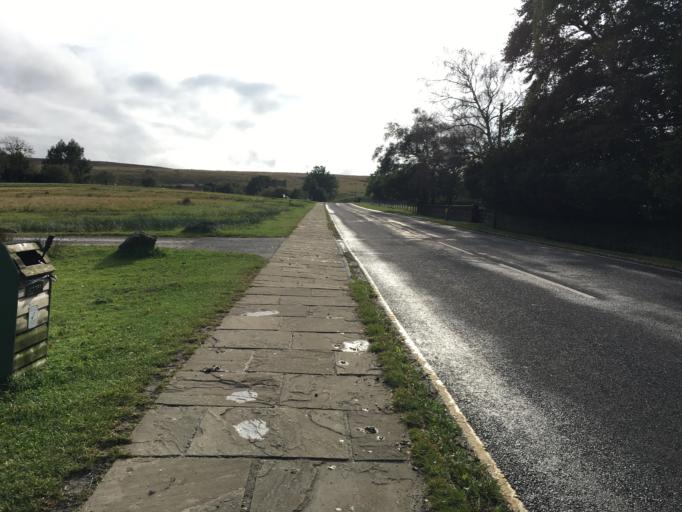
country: GB
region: England
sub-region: North Yorkshire
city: Sleights
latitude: 54.3967
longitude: -0.7242
